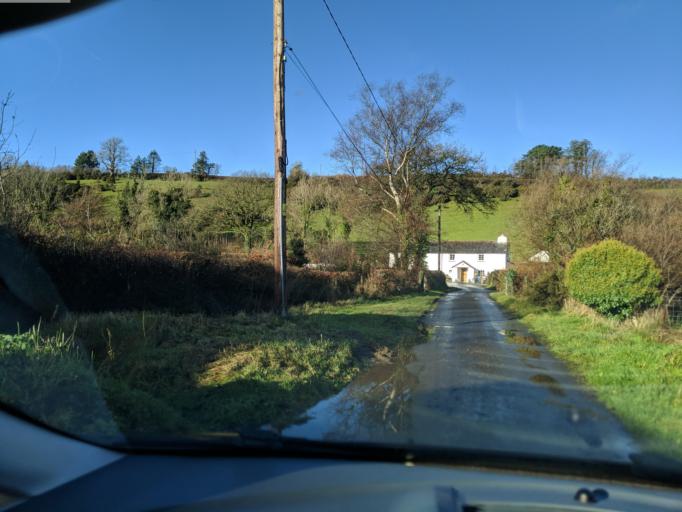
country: GB
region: England
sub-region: Devon
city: Okehampton
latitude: 50.6979
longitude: -4.0799
